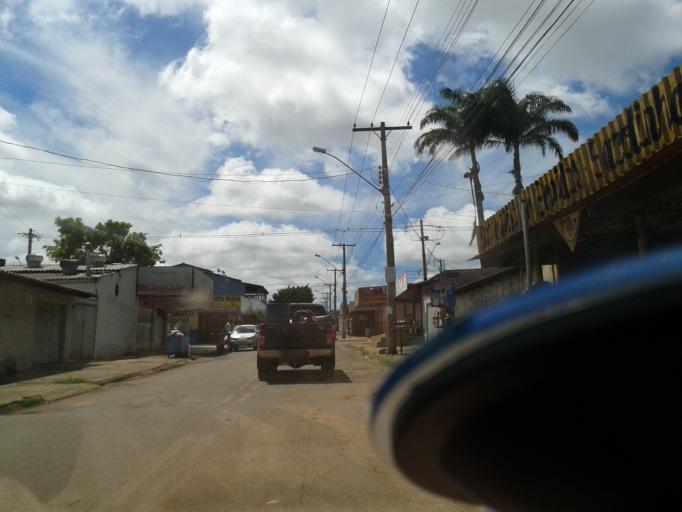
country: BR
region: Goias
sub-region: Goiania
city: Goiania
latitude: -16.6485
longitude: -49.3438
